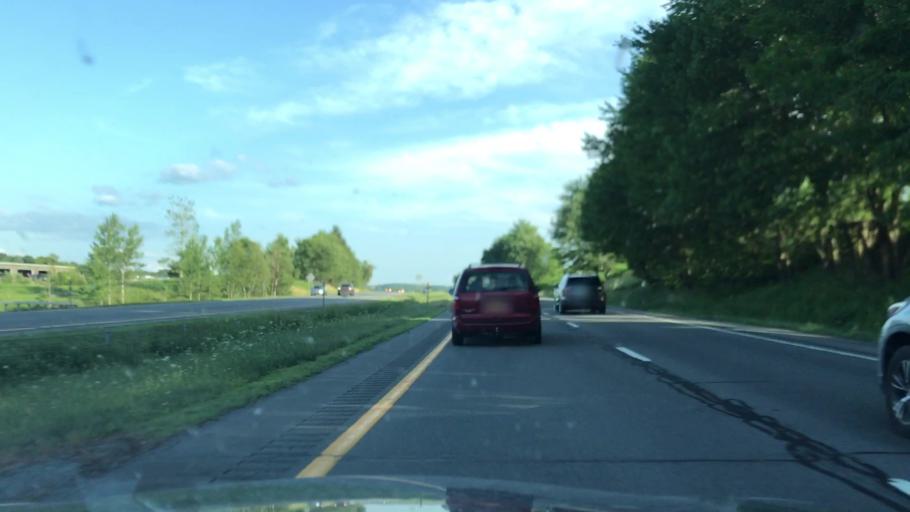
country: US
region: New York
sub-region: Sullivan County
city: Liberty
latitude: 41.7424
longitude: -74.7329
